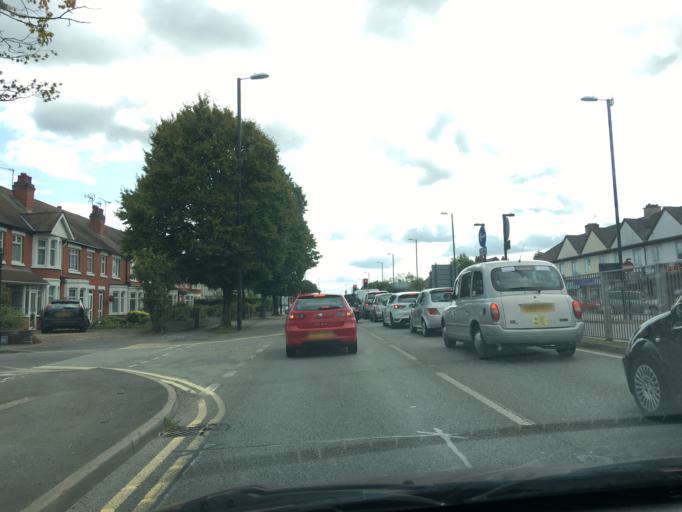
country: GB
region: England
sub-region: Coventry
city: Coventry
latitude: 52.3855
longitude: -1.5323
